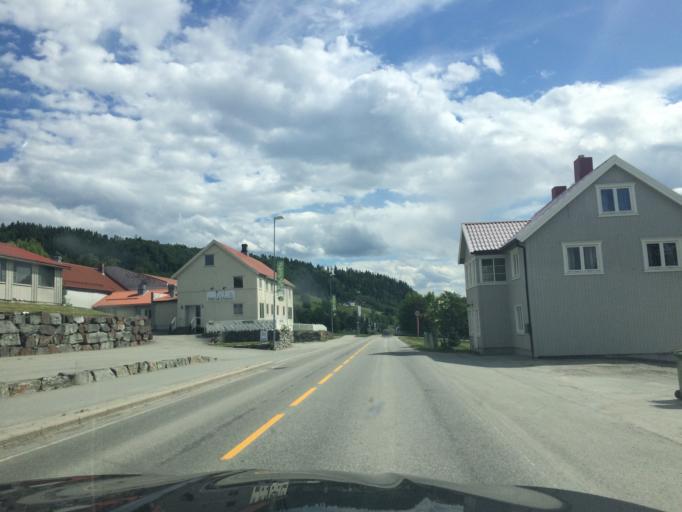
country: NO
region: Sor-Trondelag
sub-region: Selbu
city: Mebonden
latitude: 63.2213
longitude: 11.0377
